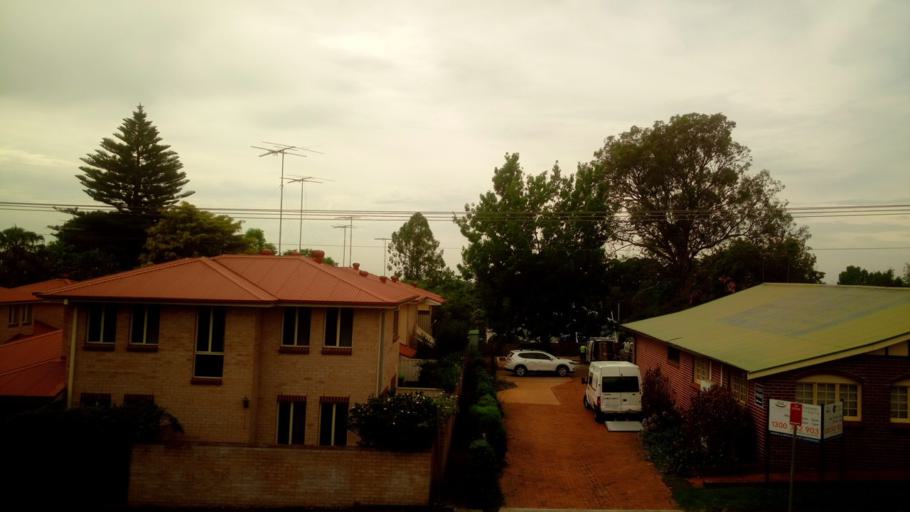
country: AU
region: New South Wales
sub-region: Blue Mountains Municipality
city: Blaxland
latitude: -33.7005
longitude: 150.5620
